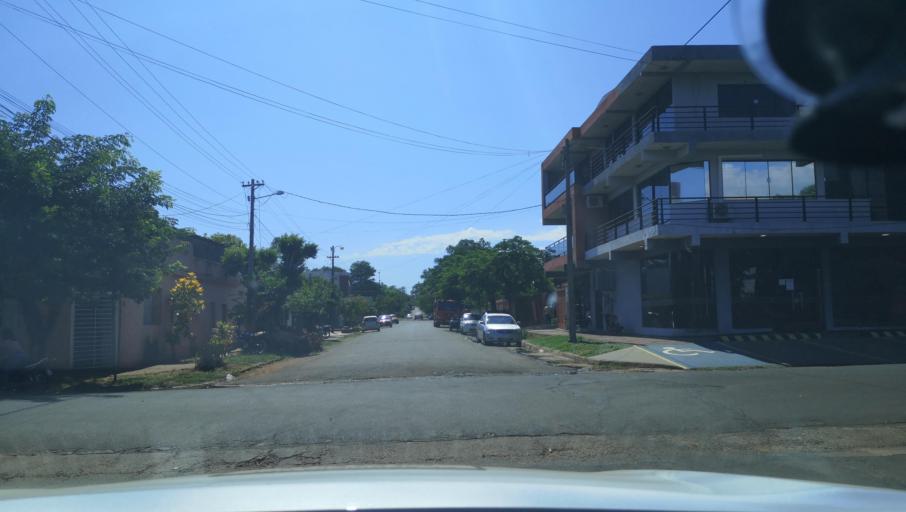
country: PY
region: Itapua
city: Carmen del Parana
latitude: -27.1591
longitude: -56.2381
